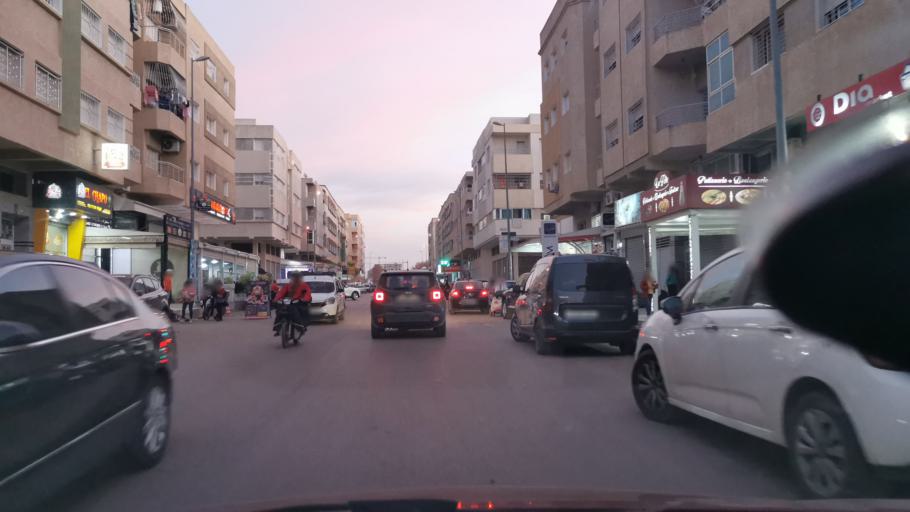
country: MA
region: Fes-Boulemane
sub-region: Fes
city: Fes
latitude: 34.0081
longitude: -4.9691
